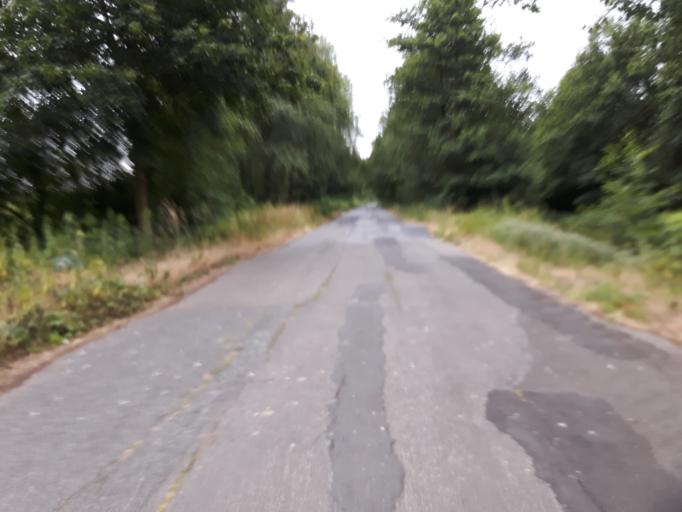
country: DE
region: Hamburg
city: Harburg
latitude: 53.4366
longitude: 10.0165
